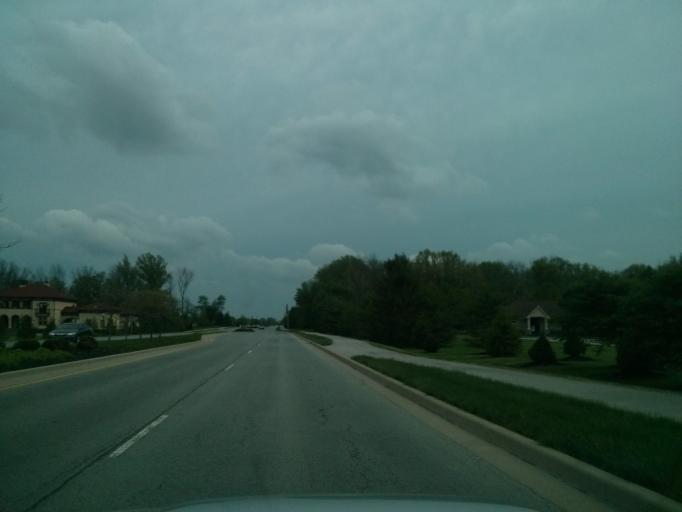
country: US
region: Indiana
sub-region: Boone County
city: Zionsville
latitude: 39.9647
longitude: -86.2027
